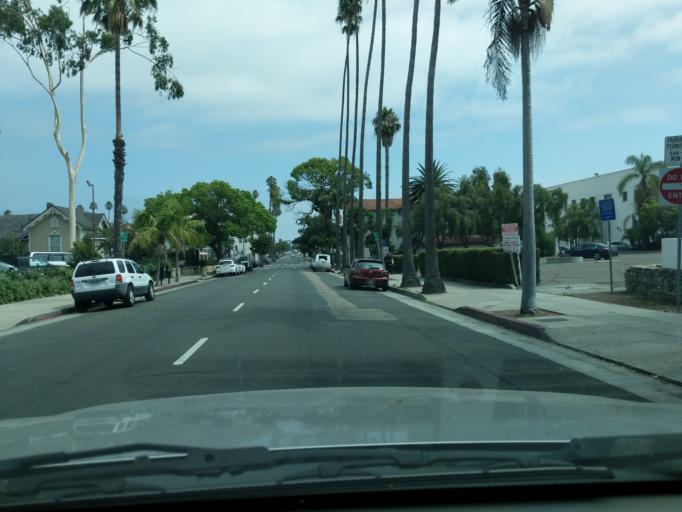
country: US
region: California
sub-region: Santa Barbara County
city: Santa Barbara
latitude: 34.4204
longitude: -119.6978
